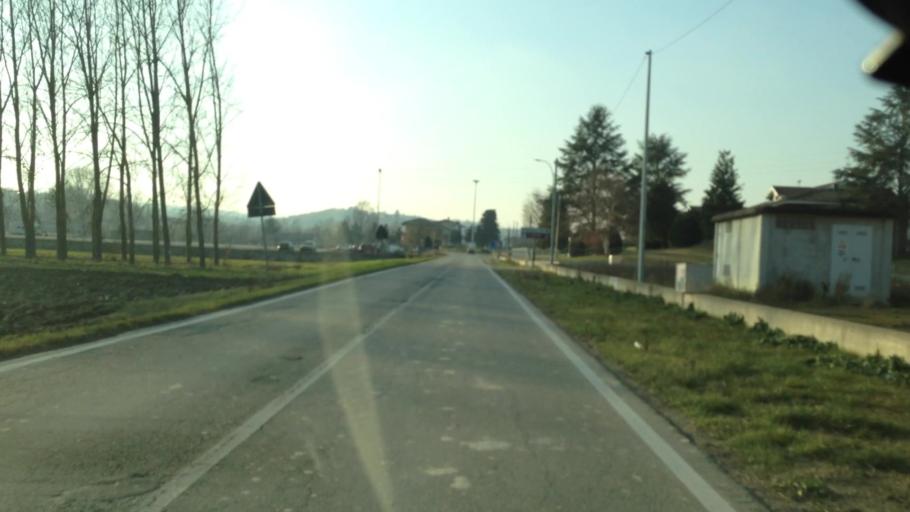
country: IT
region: Piedmont
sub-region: Provincia di Asti
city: Montaldo Scarampi
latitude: 44.8166
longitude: 8.2589
